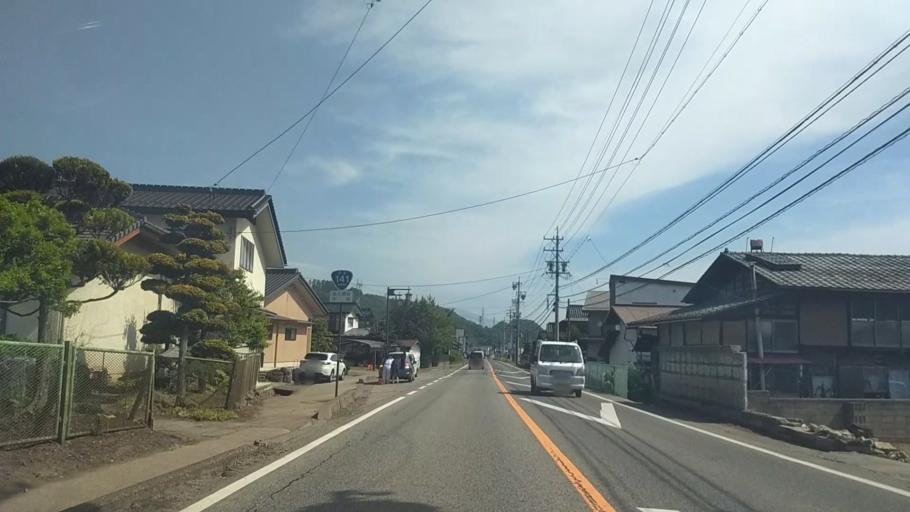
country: JP
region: Nagano
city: Saku
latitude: 36.1446
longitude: 138.4734
